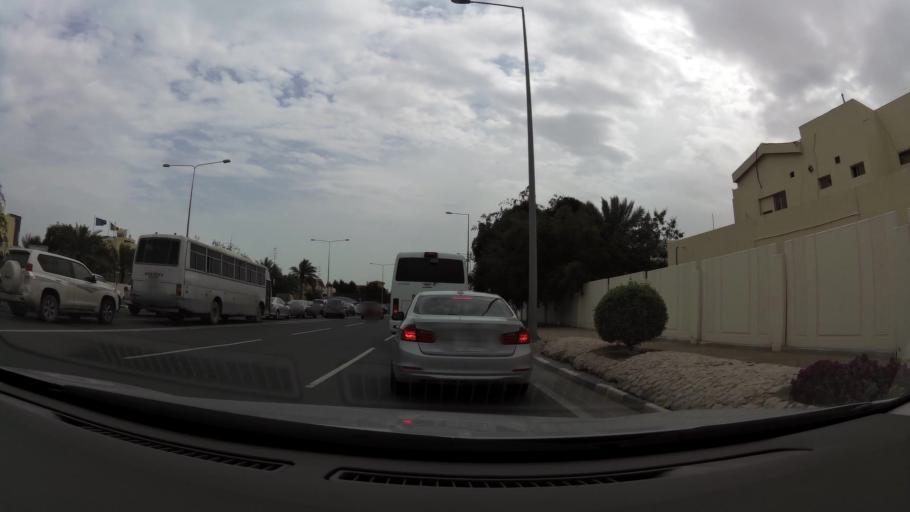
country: QA
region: Baladiyat ad Dawhah
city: Doha
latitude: 25.3314
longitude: 51.5058
